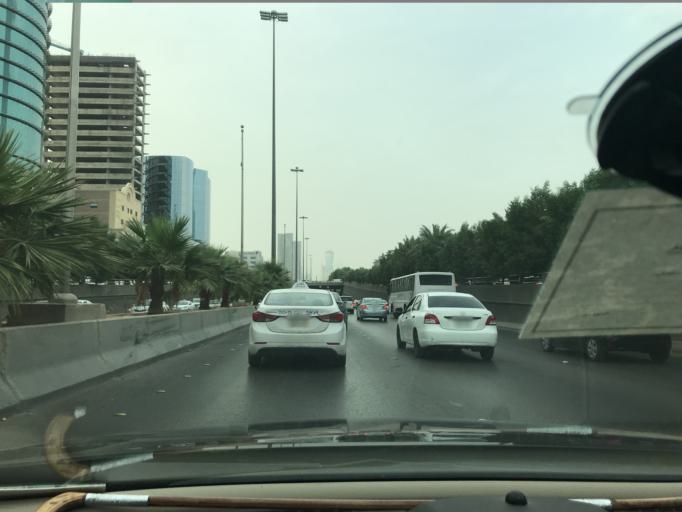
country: SA
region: Ar Riyad
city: Riyadh
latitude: 24.7095
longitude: 46.6732
